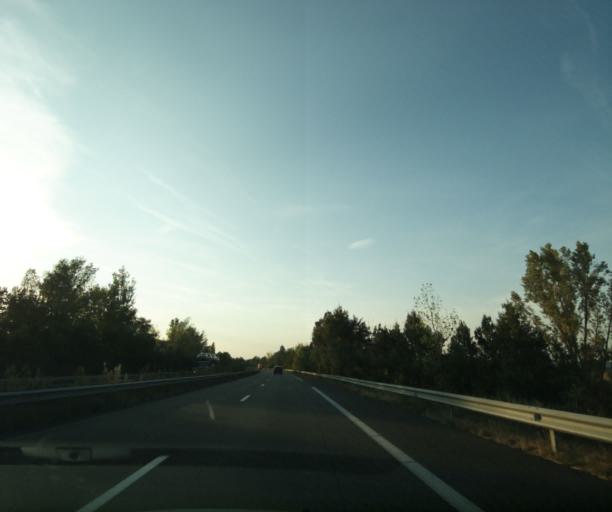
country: FR
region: Aquitaine
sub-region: Departement du Lot-et-Garonne
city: Layrac
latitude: 44.1182
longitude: 0.7223
